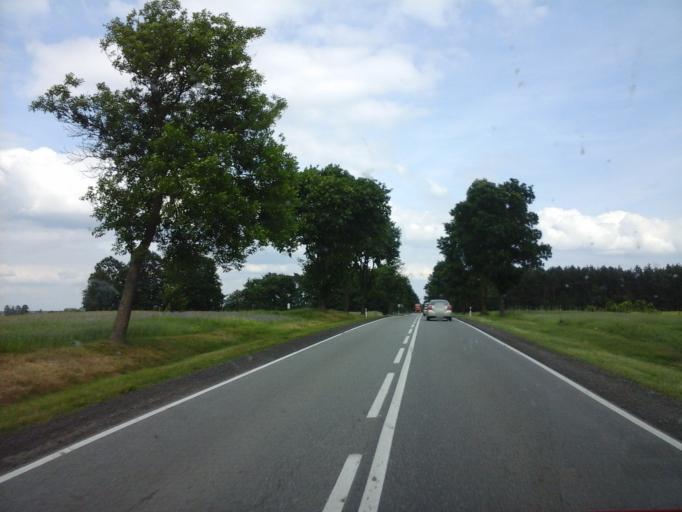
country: PL
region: Lodz Voivodeship
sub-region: Powiat opoczynski
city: Paradyz
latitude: 51.3126
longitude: 20.0805
